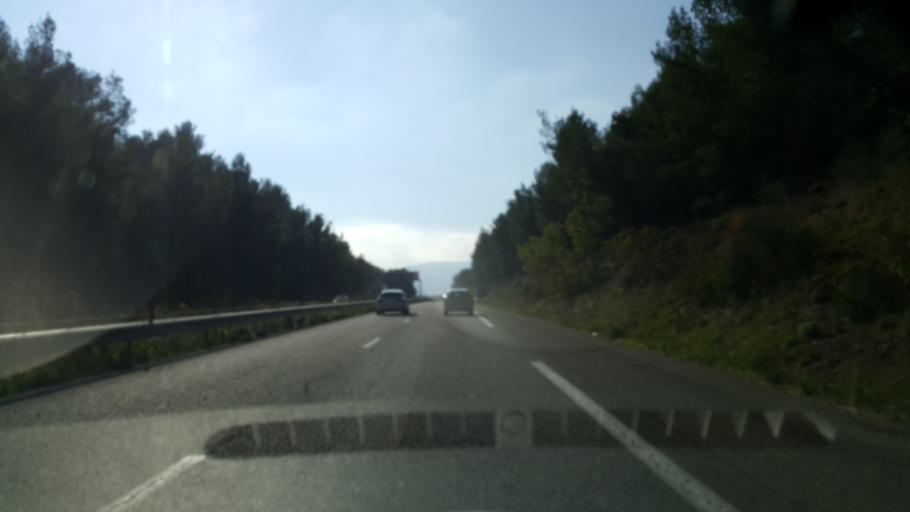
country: FR
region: Provence-Alpes-Cote d'Azur
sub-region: Departement des Bouches-du-Rhone
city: Aubagne
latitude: 43.3009
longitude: 5.5652
